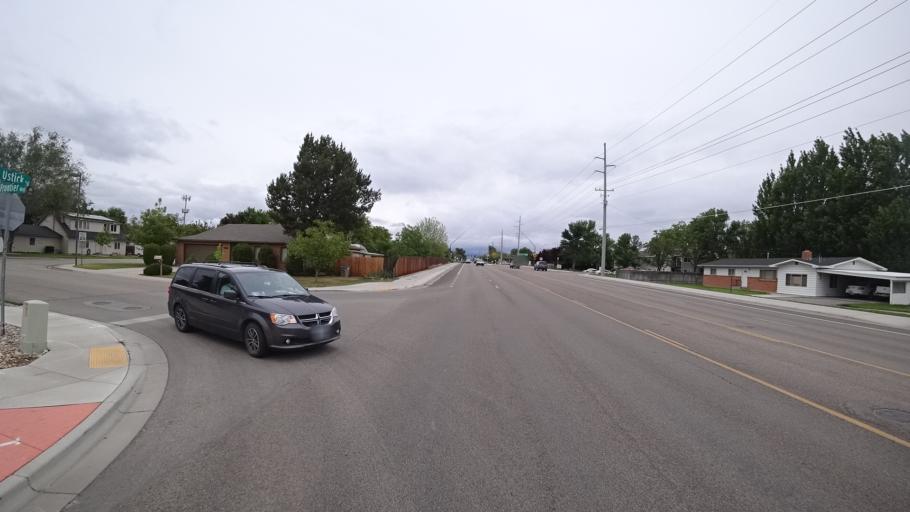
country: US
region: Idaho
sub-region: Ada County
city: Eagle
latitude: 43.6340
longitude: -116.3188
